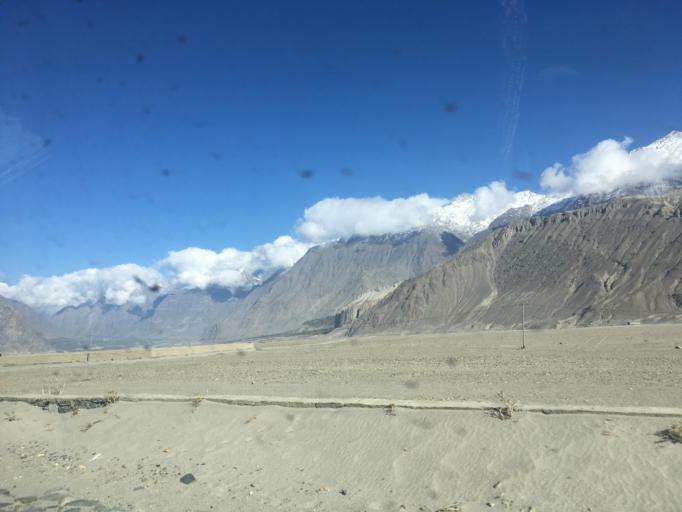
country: PK
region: Gilgit-Baltistan
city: Skardu
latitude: 35.3581
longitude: 75.5398
